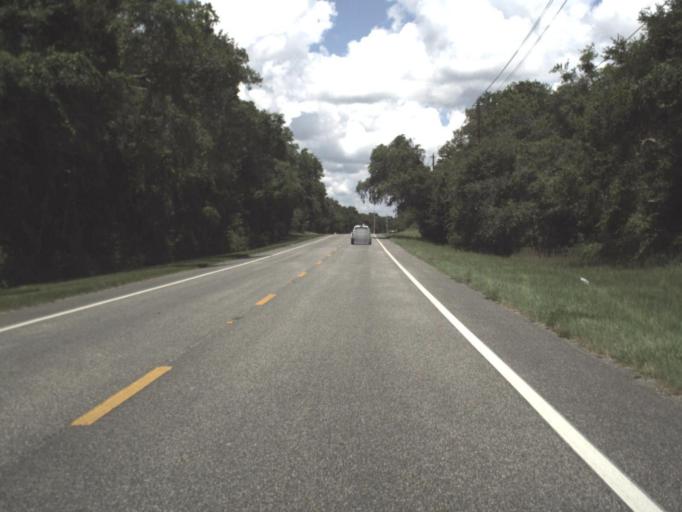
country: US
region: Florida
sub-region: Putnam County
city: Crescent City
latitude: 29.4896
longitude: -81.5800
